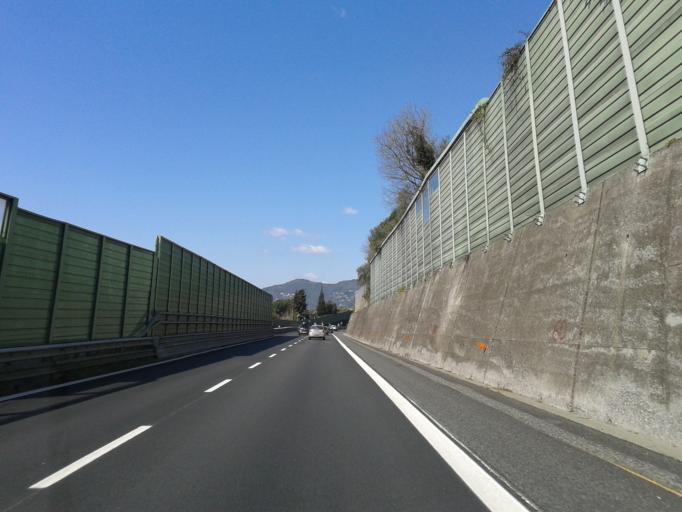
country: IT
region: Liguria
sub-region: Provincia di Genova
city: Zoagli
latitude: 44.3488
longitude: 9.2525
